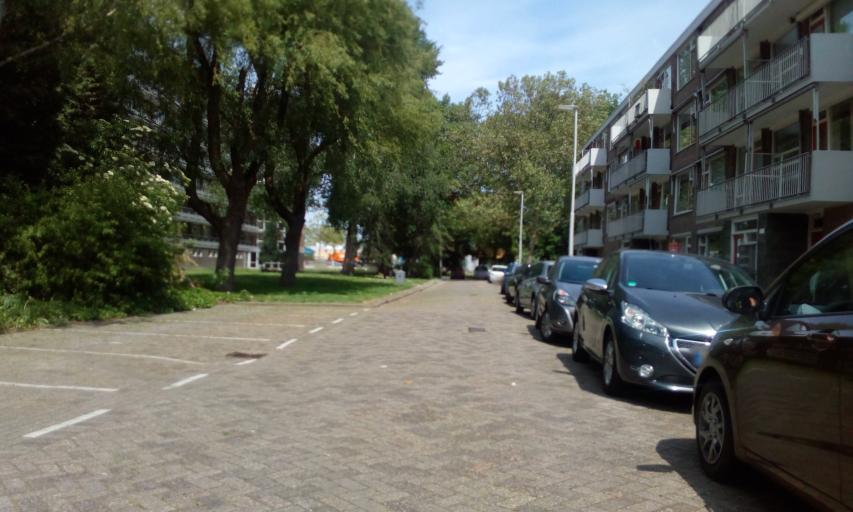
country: NL
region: South Holland
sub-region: Gemeente Rotterdam
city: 's-Gravenland
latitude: 51.9449
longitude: 4.5381
